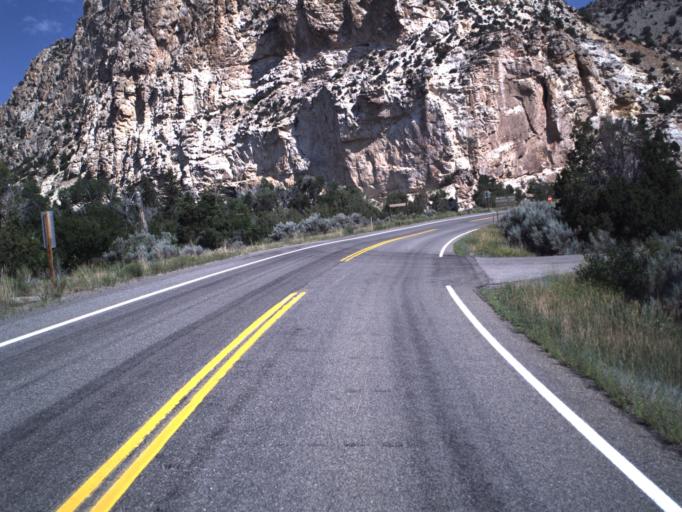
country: US
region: Utah
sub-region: Daggett County
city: Manila
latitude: 40.9279
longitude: -109.7208
